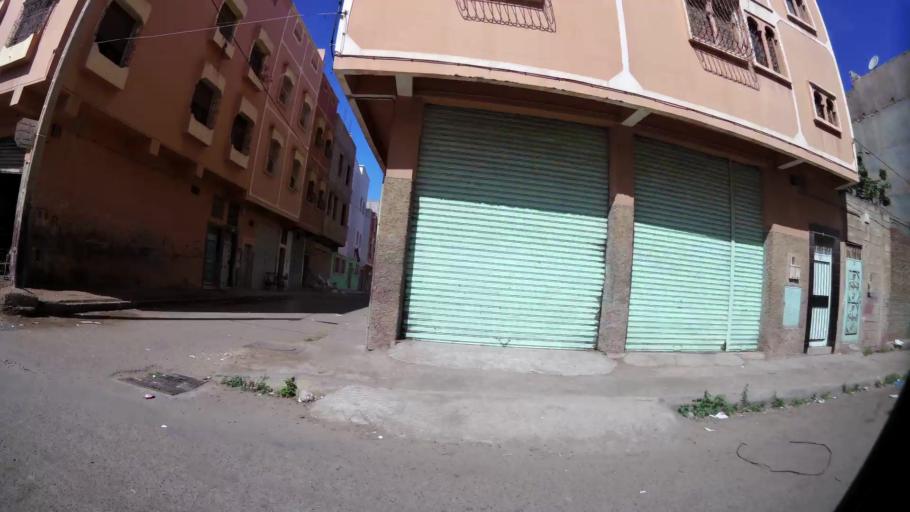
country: MA
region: Souss-Massa-Draa
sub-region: Inezgane-Ait Mellou
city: Inezgane
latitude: 30.3440
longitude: -9.5060
